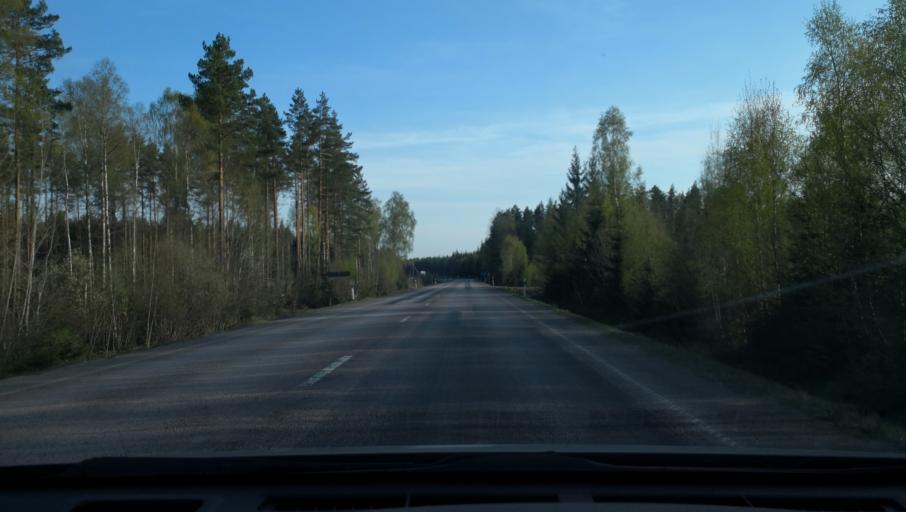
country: SE
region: Uppsala
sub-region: Heby Kommun
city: Heby
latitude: 59.9721
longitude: 16.8361
